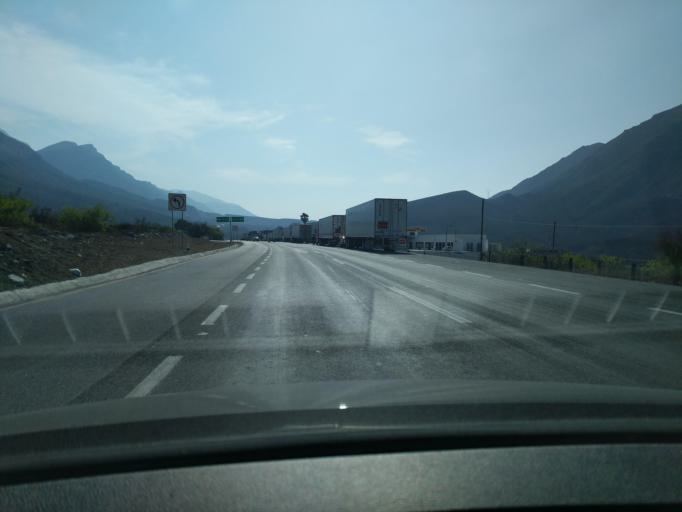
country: MX
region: Nuevo Leon
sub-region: Garcia
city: Las Torres de Guadalupe
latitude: 25.6608
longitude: -100.7137
